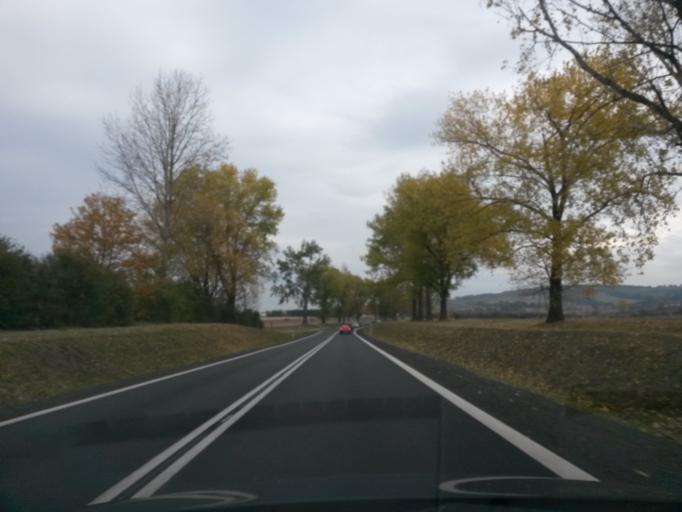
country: PL
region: Lower Silesian Voivodeship
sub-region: Powiat dzierzoniowski
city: Niemcza
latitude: 50.7033
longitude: 16.8240
